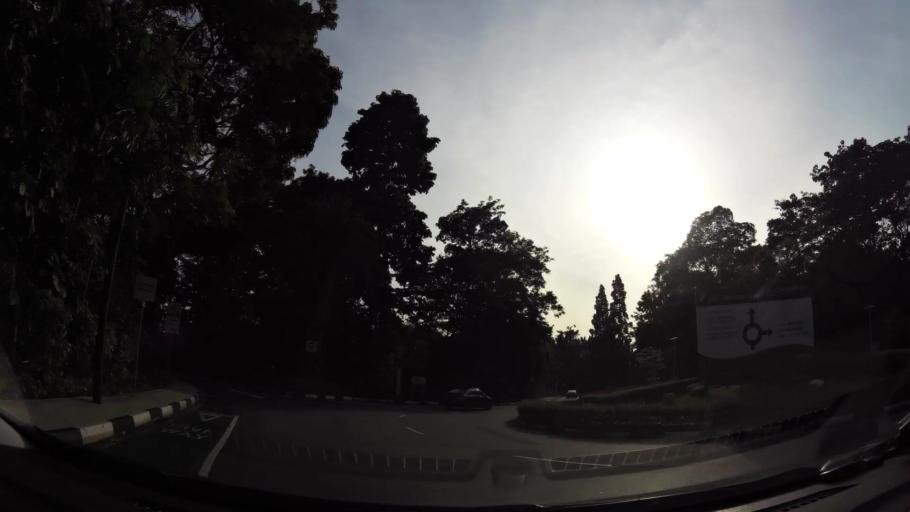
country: SG
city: Singapore
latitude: 1.2493
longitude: 103.8273
